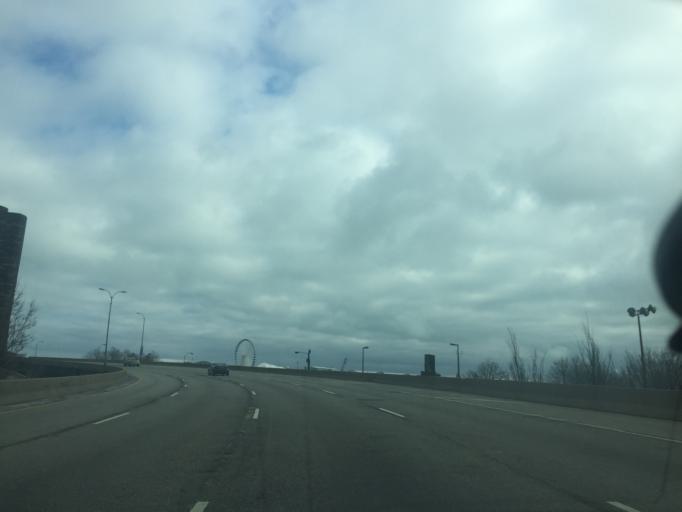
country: US
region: Illinois
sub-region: Cook County
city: Chicago
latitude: 41.8839
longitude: -87.6143
